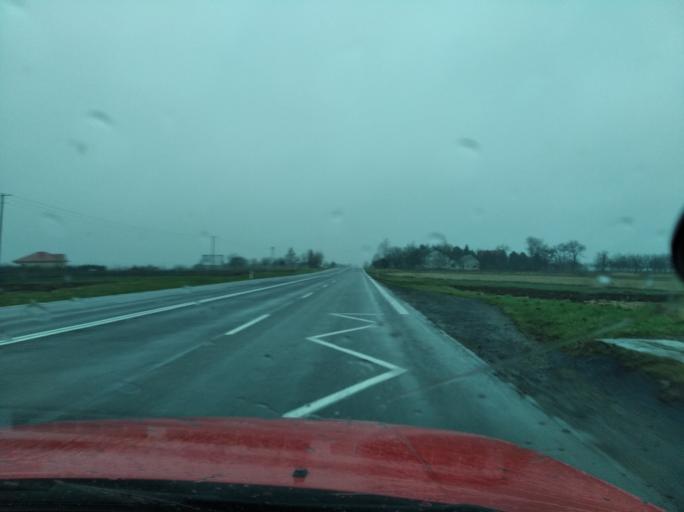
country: PL
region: Subcarpathian Voivodeship
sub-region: Powiat przeworski
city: Nowosielce
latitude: 50.0662
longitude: 22.4008
